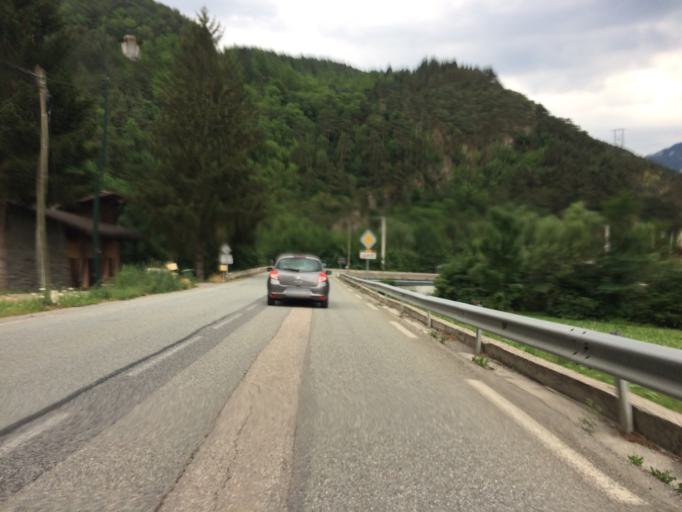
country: FR
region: Provence-Alpes-Cote d'Azur
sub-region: Departement des Alpes-Maritimes
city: Tende
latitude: 44.0743
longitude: 7.5988
